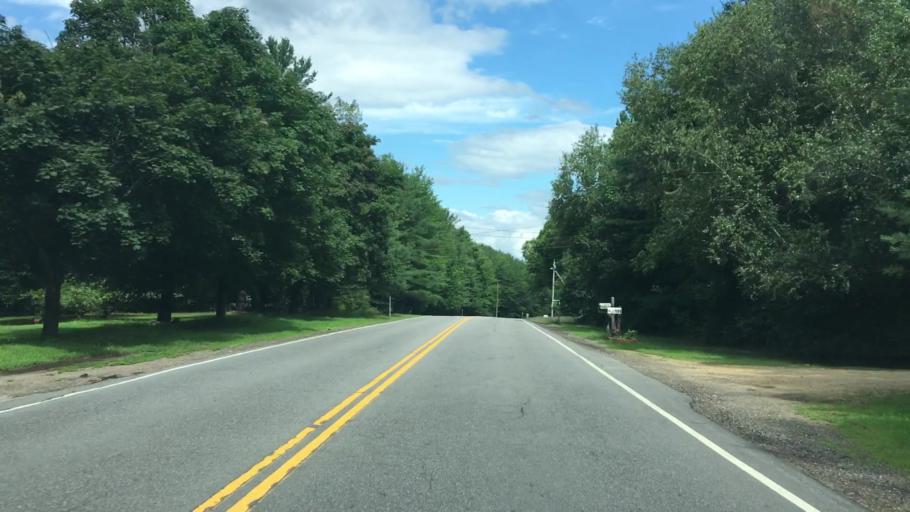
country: US
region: New Hampshire
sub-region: Belknap County
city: Meredith
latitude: 43.5863
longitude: -71.5171
